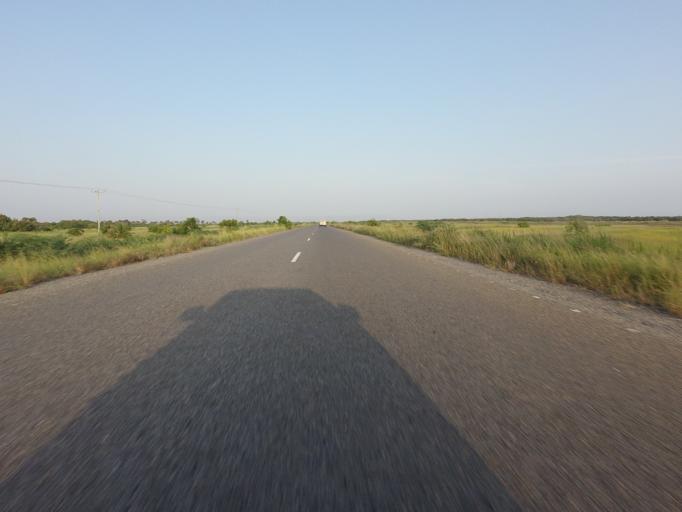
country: GH
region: Volta
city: Anloga
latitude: 5.8774
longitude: 0.7329
